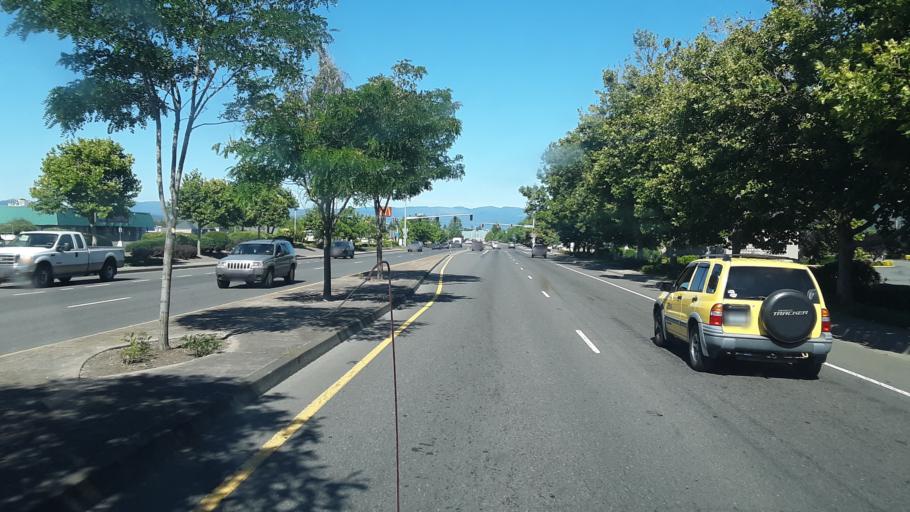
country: US
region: Oregon
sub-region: Josephine County
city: Fruitdale
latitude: 42.4368
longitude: -123.3055
